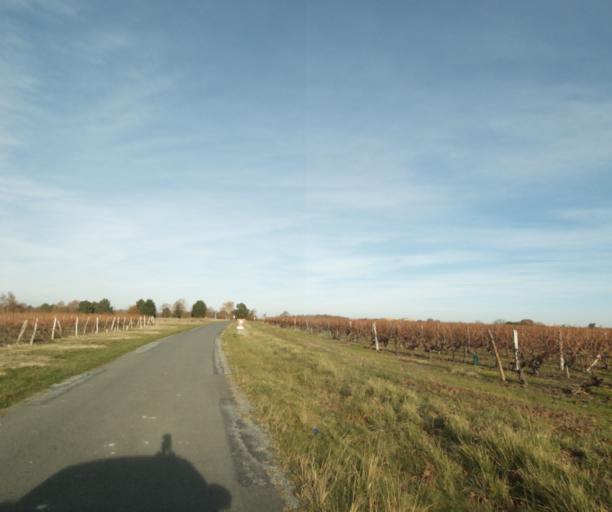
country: FR
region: Poitou-Charentes
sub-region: Departement de la Charente-Maritime
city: Chaniers
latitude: 45.7515
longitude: -0.5193
